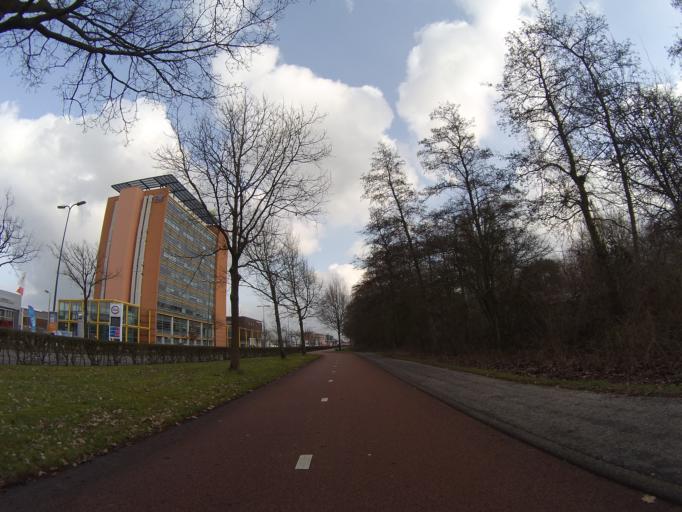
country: NL
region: Utrecht
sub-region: Gemeente Amersfoort
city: Hoogland
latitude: 52.1643
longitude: 5.3609
